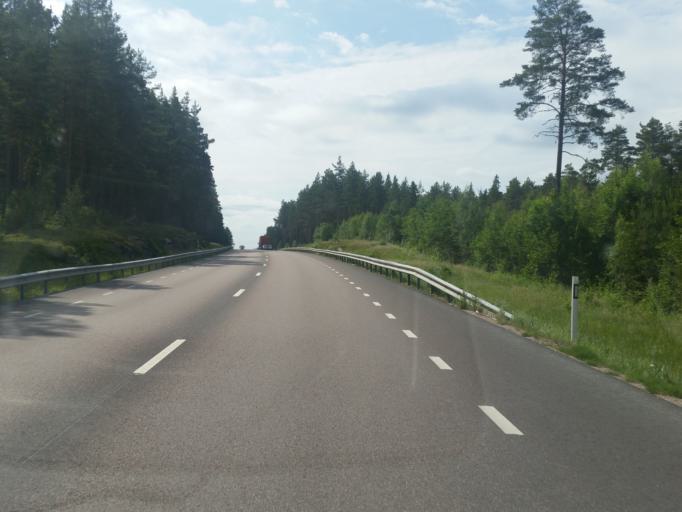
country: SE
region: Dalarna
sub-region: Gagnefs Kommun
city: Gagnef
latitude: 60.6420
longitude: 15.0578
